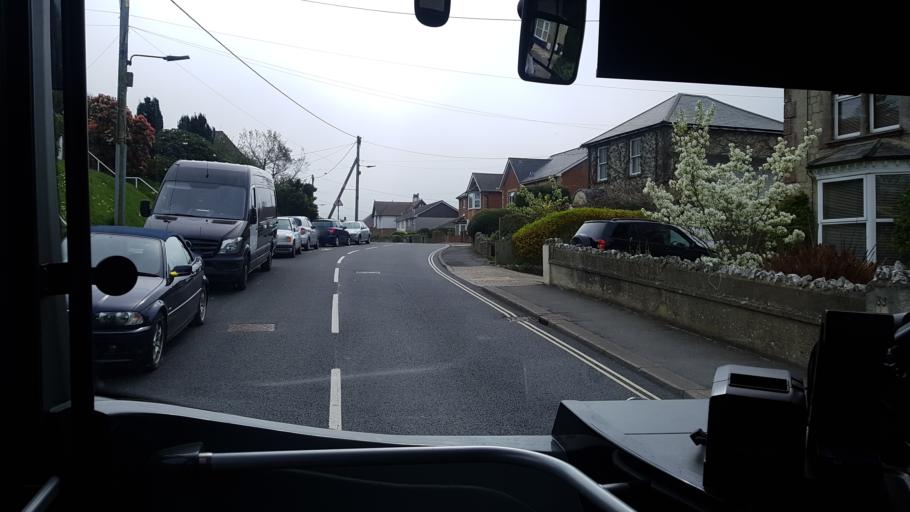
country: GB
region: England
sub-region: Isle of Wight
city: Ventnor
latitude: 50.6126
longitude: -1.2238
